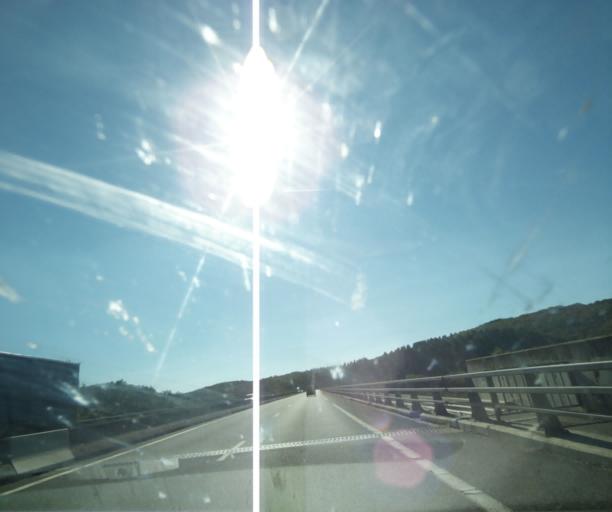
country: FR
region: Midi-Pyrenees
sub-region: Departement du Lot
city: Souillac
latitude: 44.8533
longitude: 1.4965
